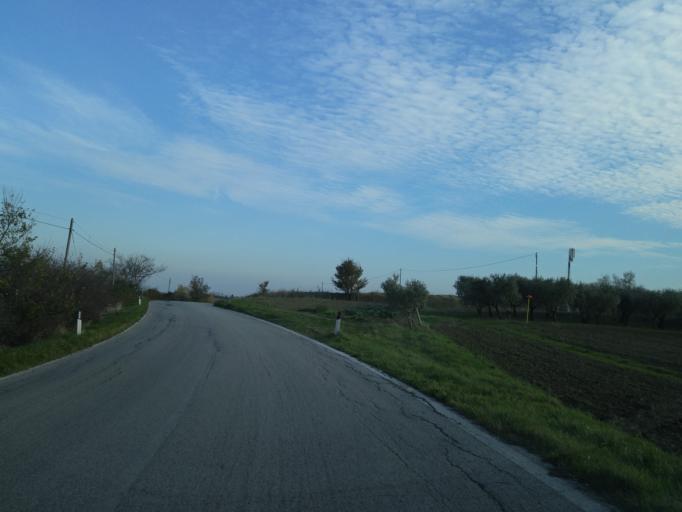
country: IT
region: The Marches
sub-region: Provincia di Pesaro e Urbino
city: Lucrezia
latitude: 43.7980
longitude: 12.9151
